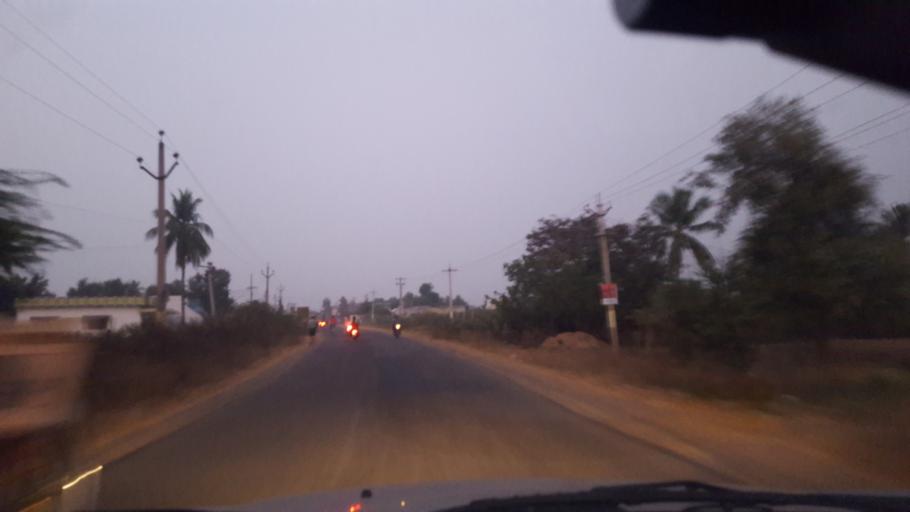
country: IN
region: Andhra Pradesh
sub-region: Srikakulam
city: Palasa
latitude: 18.7449
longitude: 84.4147
